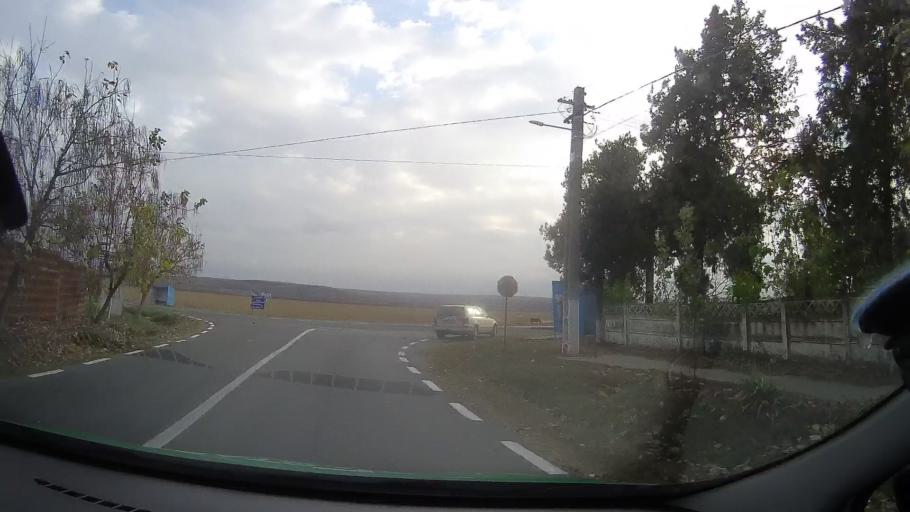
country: RO
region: Constanta
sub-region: Comuna Mircea Voda
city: Mircea Voda
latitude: 44.2715
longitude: 28.1721
